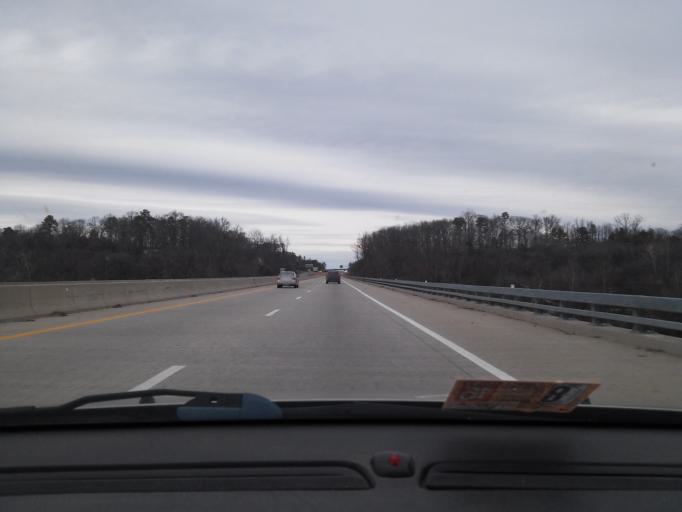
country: US
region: Virginia
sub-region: Henrico County
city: Short Pump
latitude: 37.5752
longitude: -77.6801
